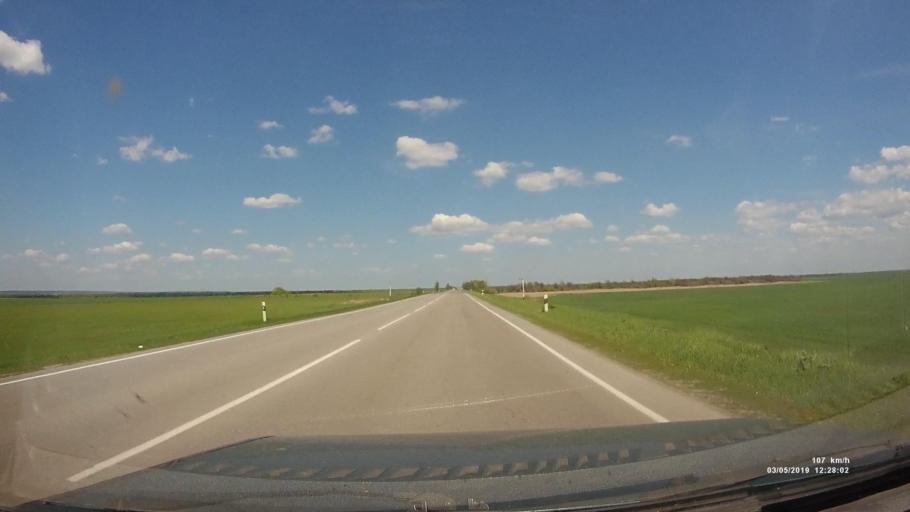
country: RU
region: Rostov
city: Semikarakorsk
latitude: 47.4673
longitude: 40.7251
